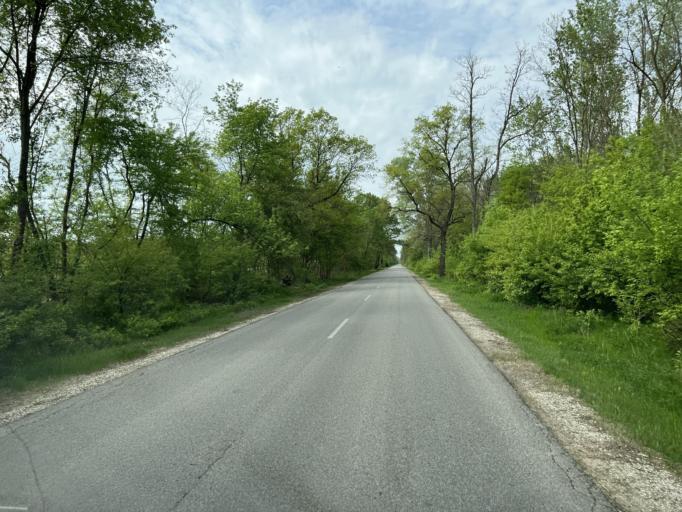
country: HU
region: Pest
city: Csemo
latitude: 47.1488
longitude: 19.6240
